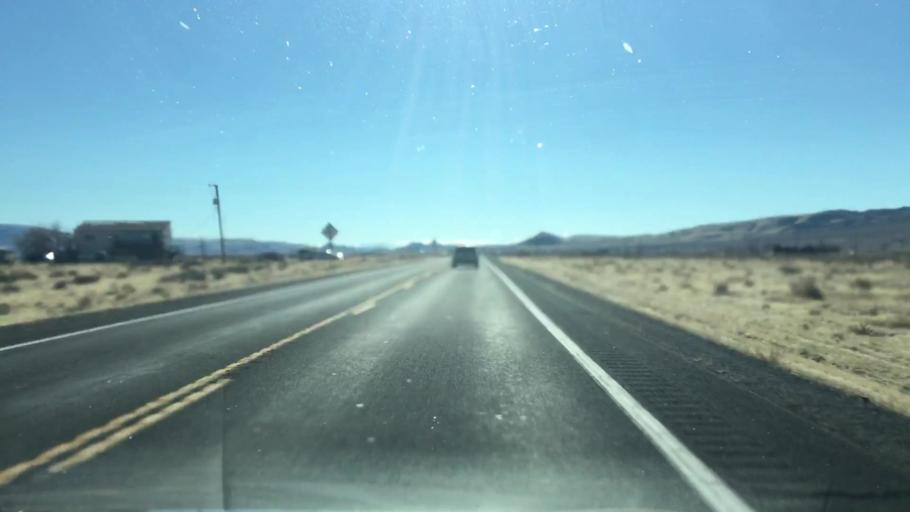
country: US
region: Nevada
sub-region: Lyon County
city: Silver Springs
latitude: 39.3888
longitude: -119.2308
